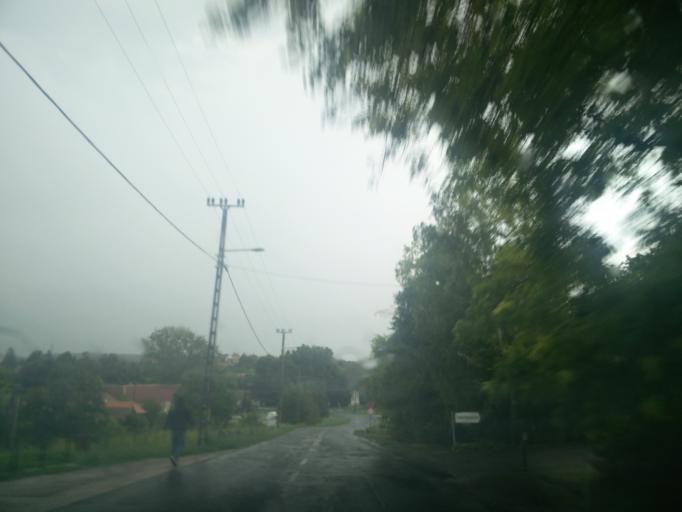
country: HU
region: Fejer
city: Etyek
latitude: 47.4443
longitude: 18.7468
